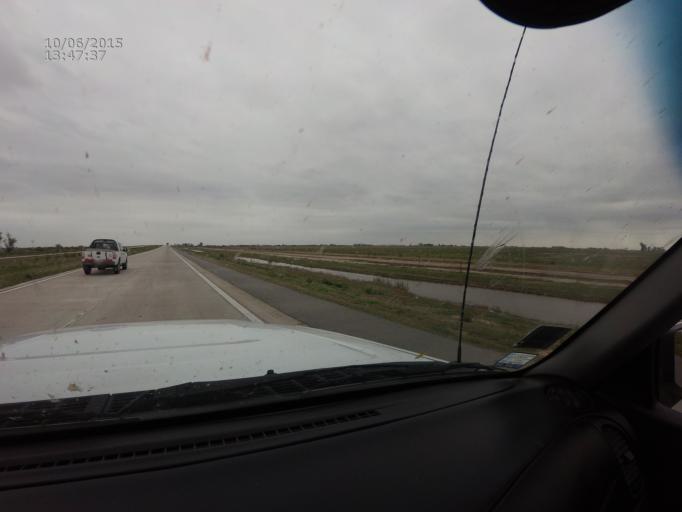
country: AR
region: Cordoba
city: Bell Ville
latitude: -32.5805
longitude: -62.6286
